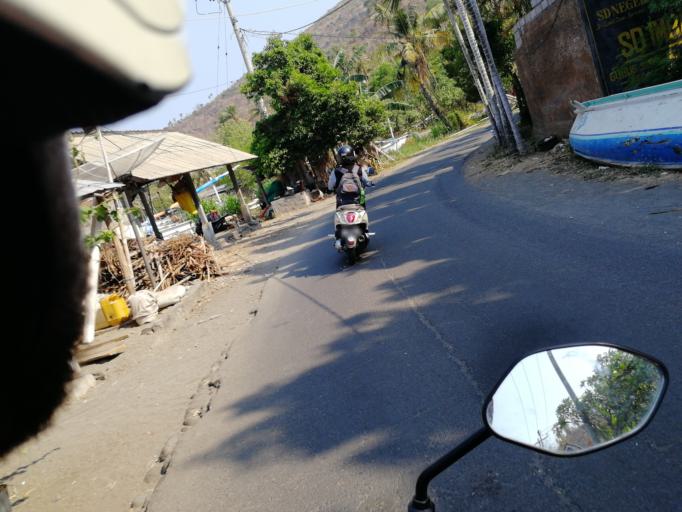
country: ID
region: Bali
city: Biaslantang Kaler
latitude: -8.3539
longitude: 115.6881
